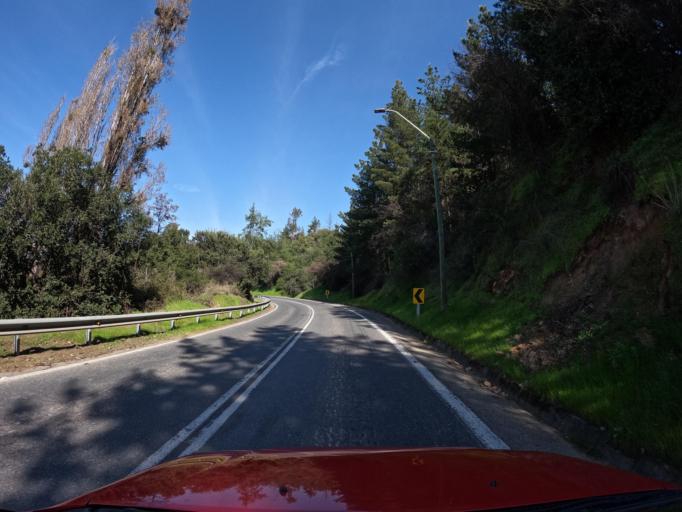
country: CL
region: Maule
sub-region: Provincia de Curico
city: Rauco
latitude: -34.9902
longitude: -71.4400
